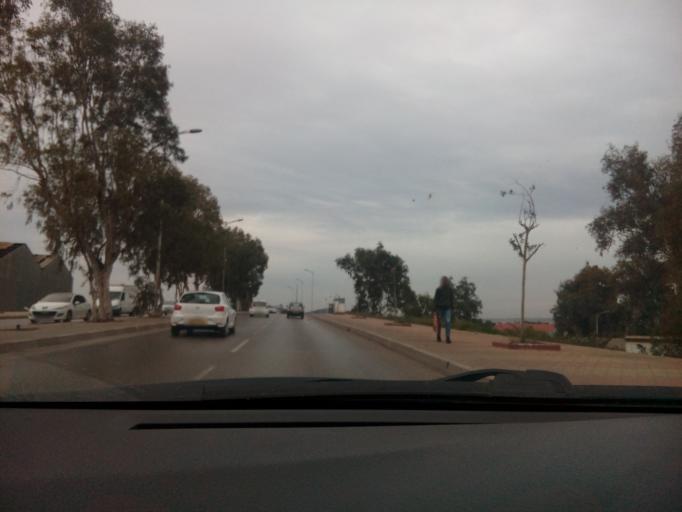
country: DZ
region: Oran
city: Oran
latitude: 35.6755
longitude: -0.6214
